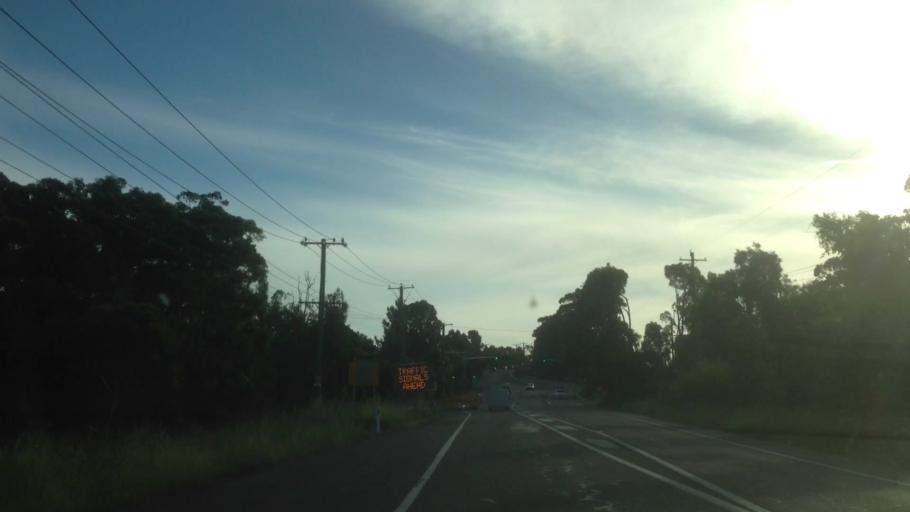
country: AU
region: New South Wales
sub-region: Lake Macquarie Shire
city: Dora Creek
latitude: -33.1054
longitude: 151.4988
